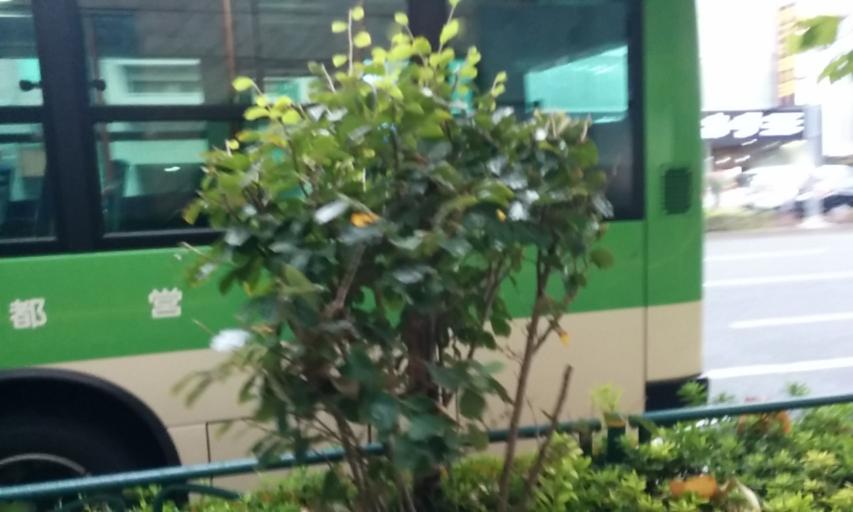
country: JP
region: Tokyo
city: Tokyo
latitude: 35.7061
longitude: 139.7541
